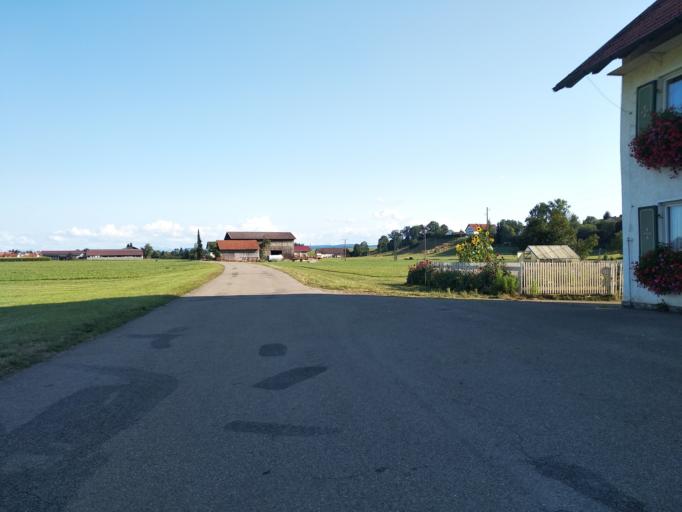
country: DE
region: Bavaria
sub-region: Swabia
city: Legau
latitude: 47.8694
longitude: 10.1185
